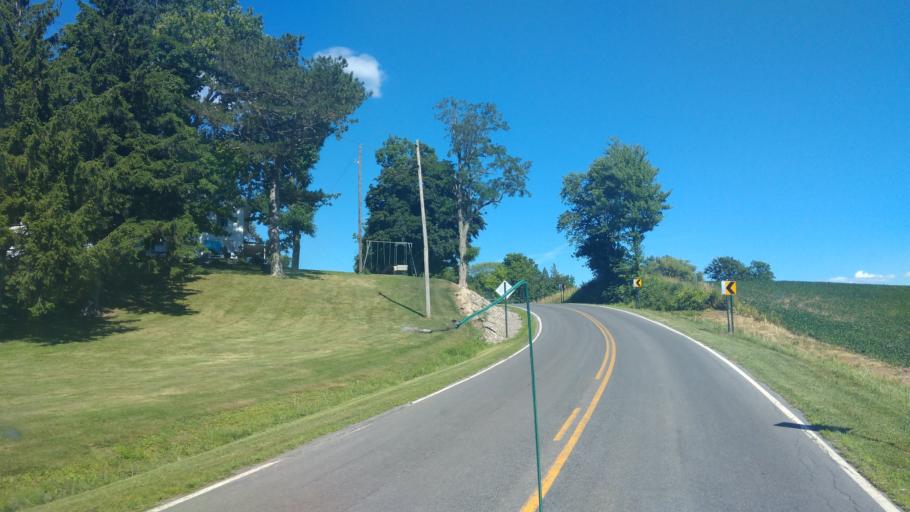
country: US
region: New York
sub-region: Wayne County
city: Clyde
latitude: 43.0205
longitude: -76.8151
